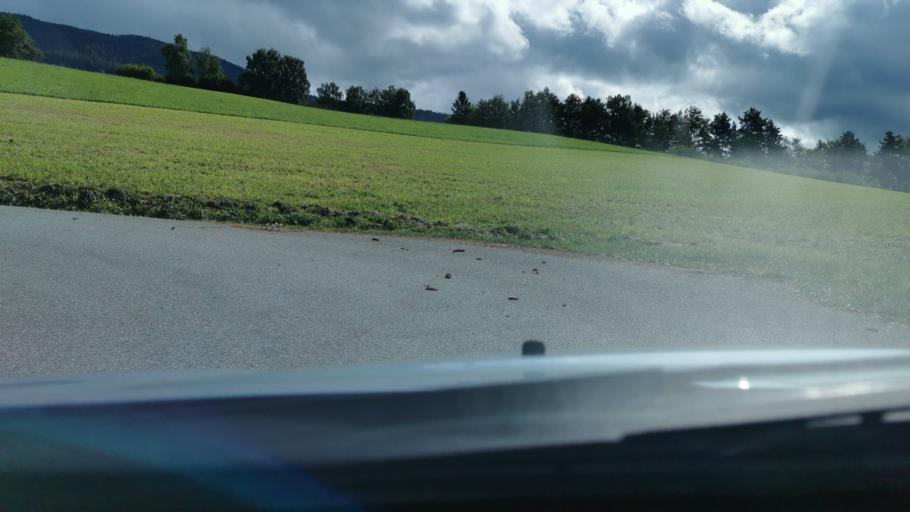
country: AT
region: Styria
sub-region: Politischer Bezirk Weiz
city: Baierdorf-Umgebung
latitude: 47.3006
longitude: 15.7041
